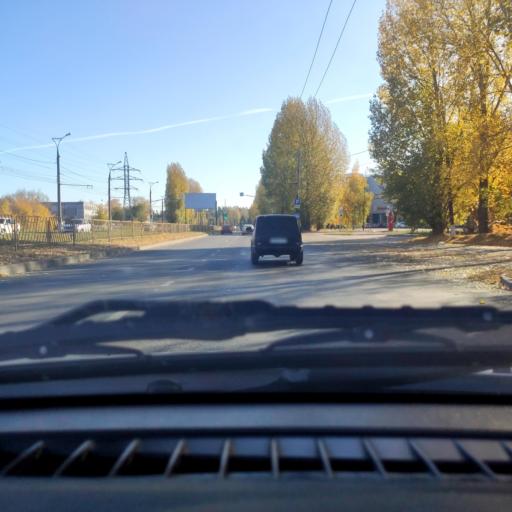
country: RU
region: Samara
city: Tol'yatti
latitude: 53.5123
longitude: 49.4550
